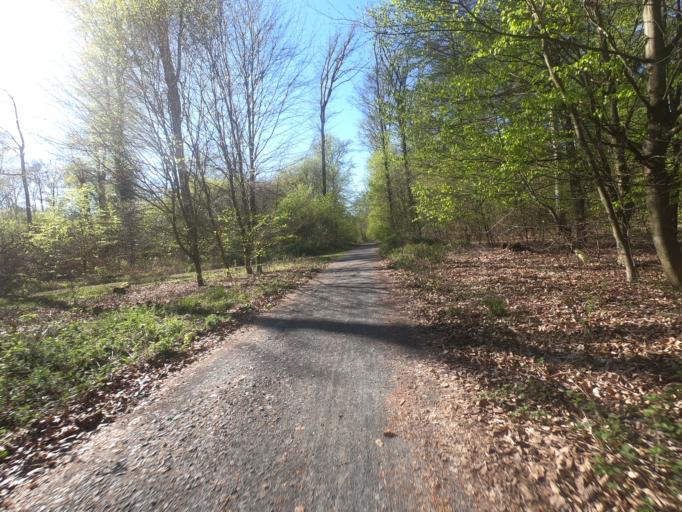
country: DE
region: Hesse
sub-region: Regierungsbezirk Darmstadt
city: Egelsbach
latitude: 49.9779
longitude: 8.7034
